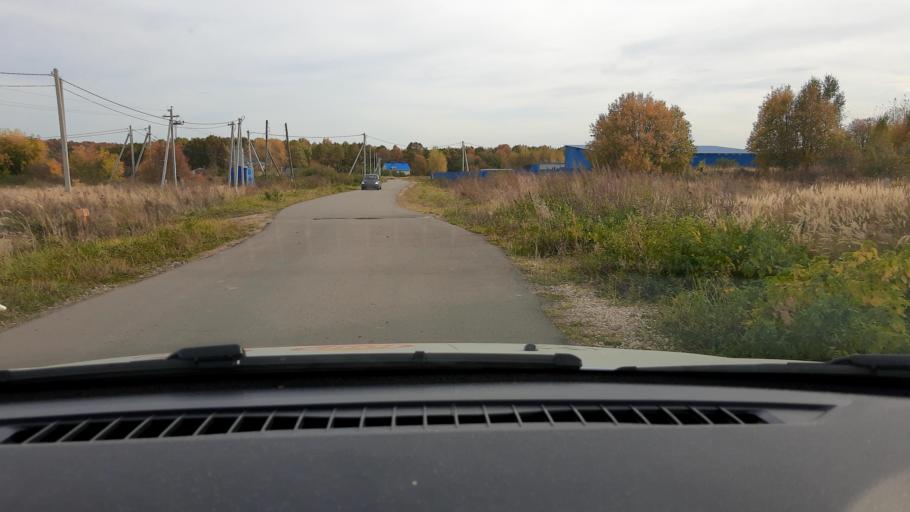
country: RU
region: Nizjnij Novgorod
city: Babino
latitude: 56.1304
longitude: 43.6462
